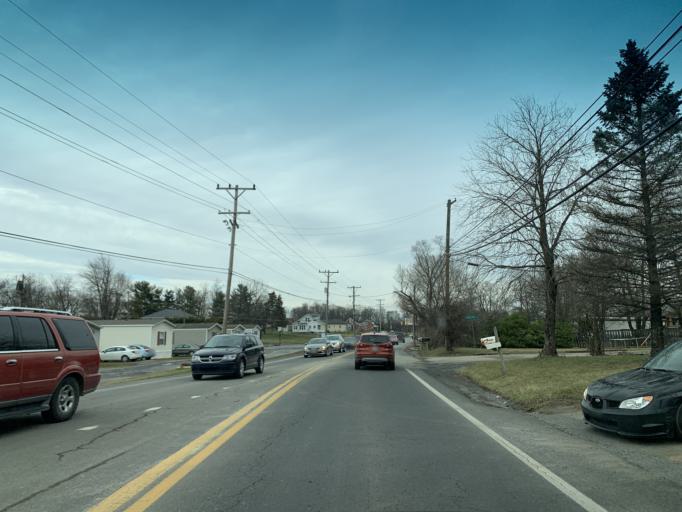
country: US
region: West Virginia
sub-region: Berkeley County
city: Martinsburg
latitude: 39.4959
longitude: -77.9425
